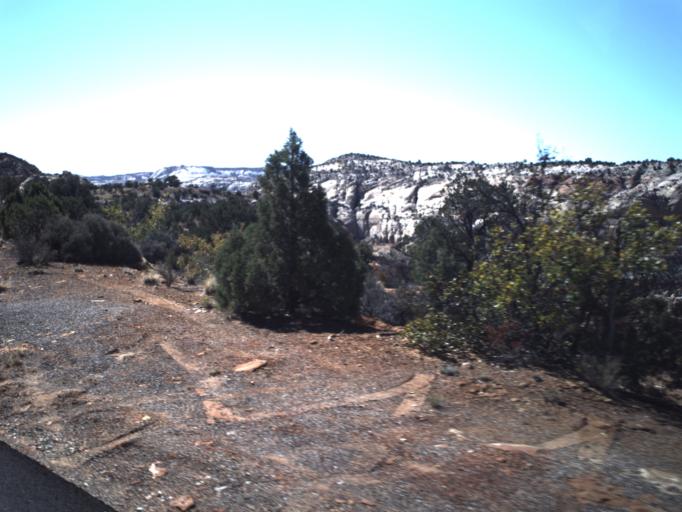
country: US
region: Utah
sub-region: Wayne County
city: Loa
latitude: 37.8008
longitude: -111.4065
